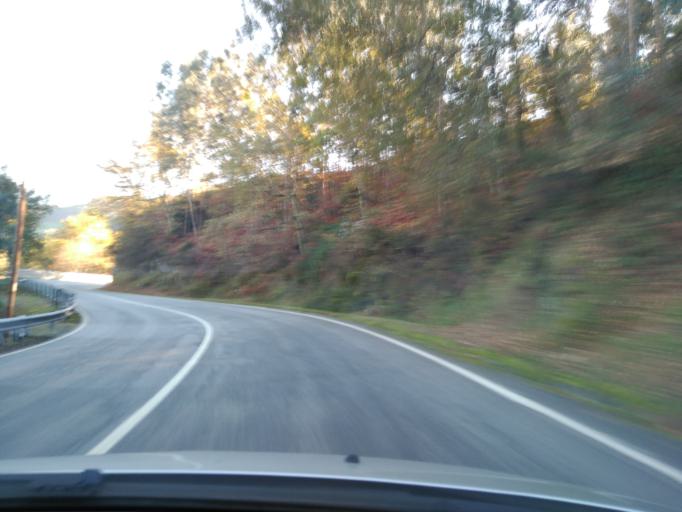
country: PT
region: Braga
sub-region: Vieira do Minho
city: Vieira do Minho
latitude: 41.6806
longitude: -8.1084
